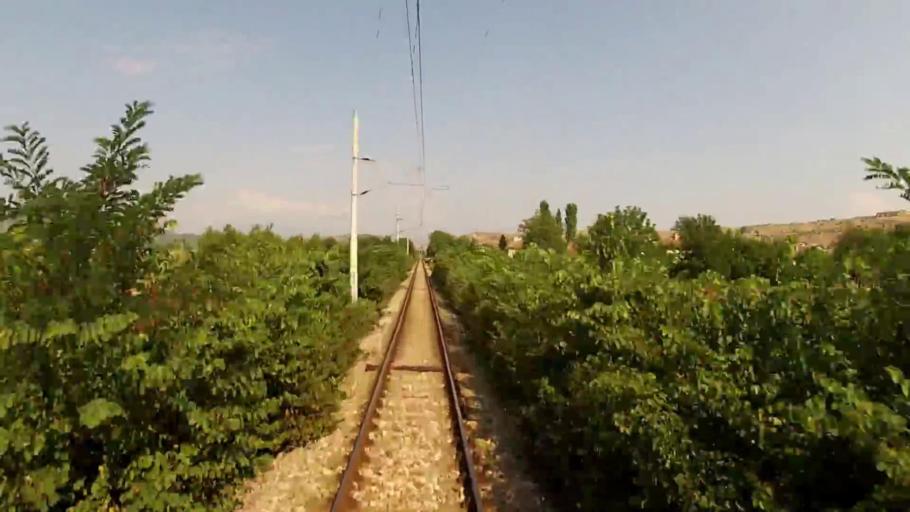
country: BG
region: Blagoevgrad
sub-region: Obshtina Petrich
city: Petrich
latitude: 41.4149
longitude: 23.3394
